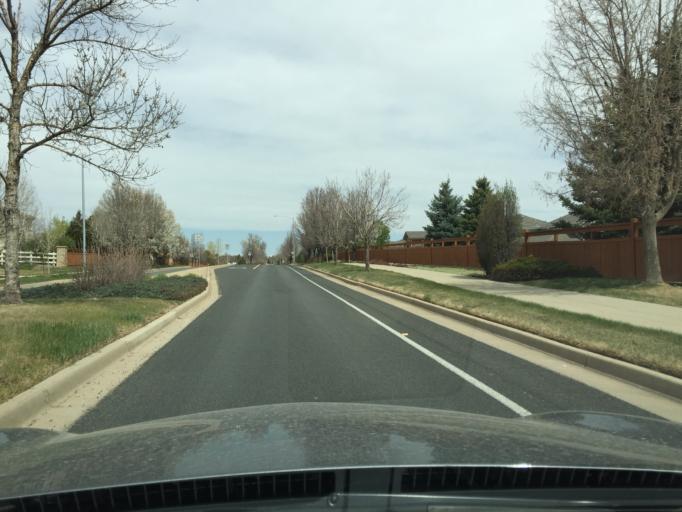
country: US
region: Colorado
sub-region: Broomfield County
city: Broomfield
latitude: 39.9480
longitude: -105.0344
